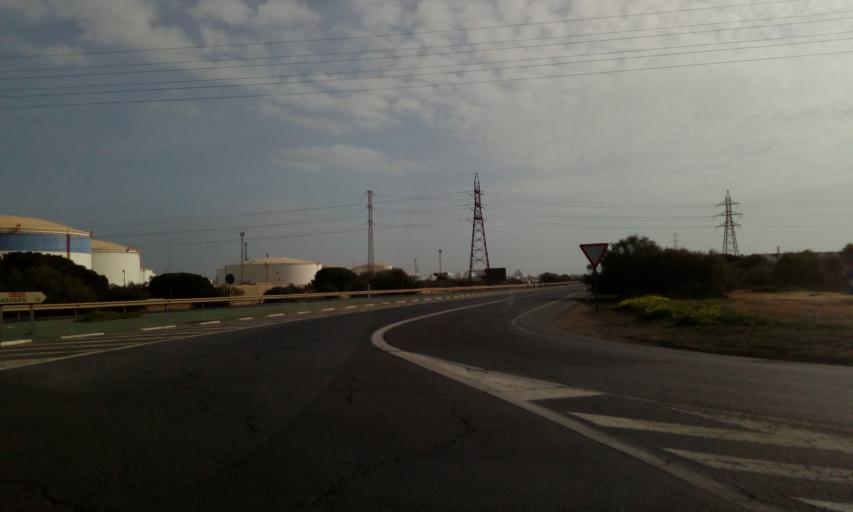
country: ES
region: Andalusia
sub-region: Provincia de Huelva
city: Punta Umbria
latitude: 37.1953
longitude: -6.9255
